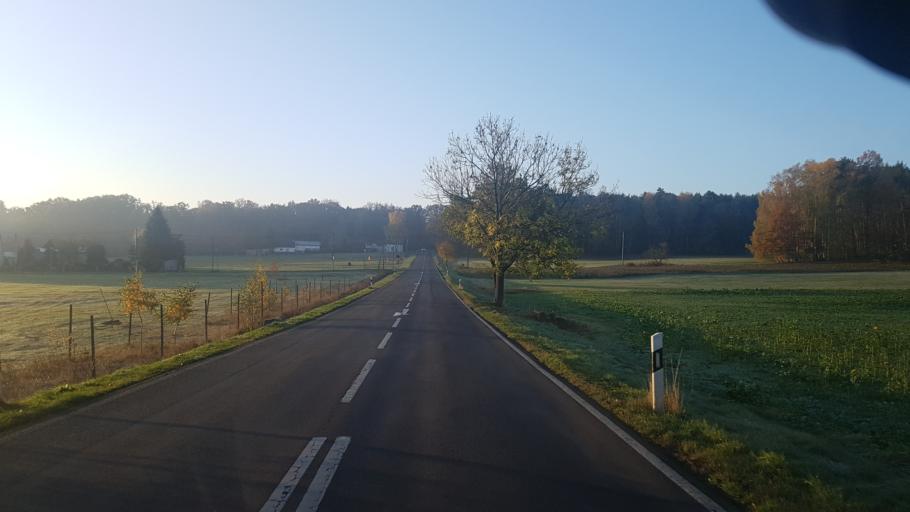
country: DE
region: Saxony
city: Schildau
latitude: 51.4300
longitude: 12.9716
